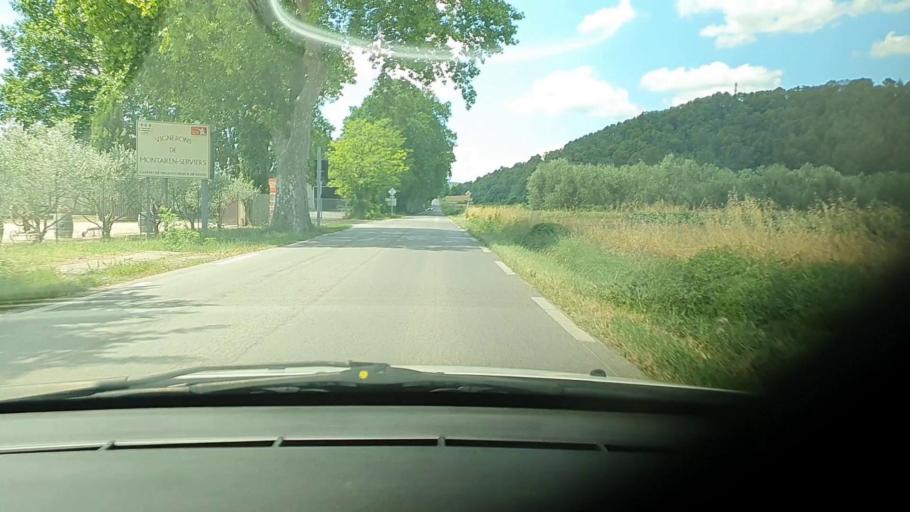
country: FR
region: Languedoc-Roussillon
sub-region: Departement du Gard
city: Montaren-et-Saint-Mediers
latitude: 44.0307
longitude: 4.3735
